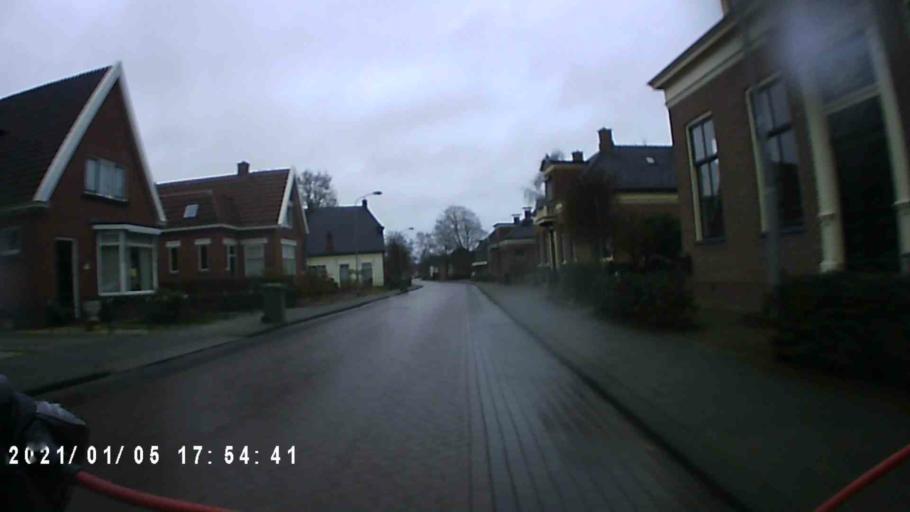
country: NL
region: Groningen
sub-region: Gemeente Slochteren
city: Slochteren
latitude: 53.2019
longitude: 6.8732
